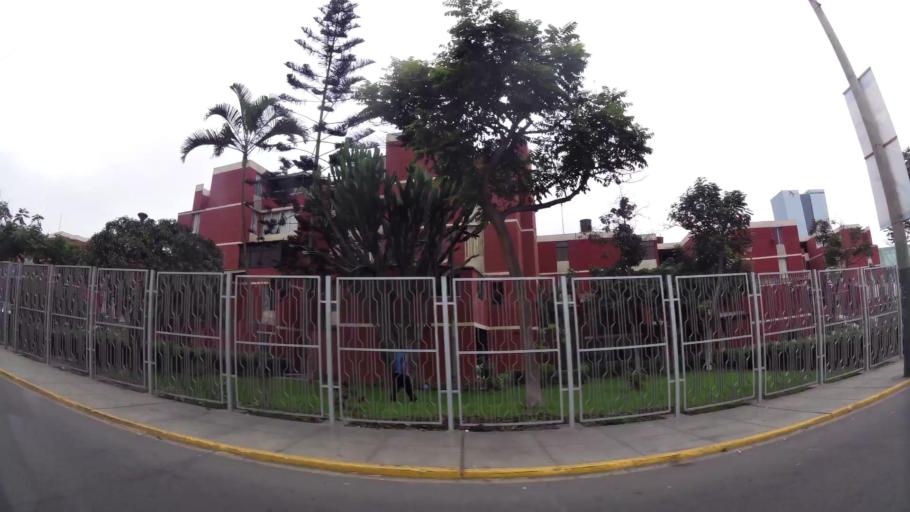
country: PE
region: Lima
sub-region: Lima
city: San Luis
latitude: -12.0834
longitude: -76.9988
